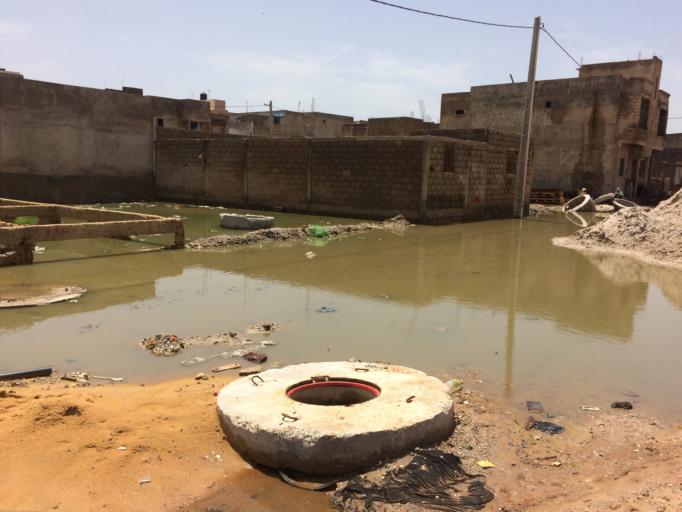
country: SN
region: Dakar
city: Pikine
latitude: 14.7359
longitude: -17.3372
